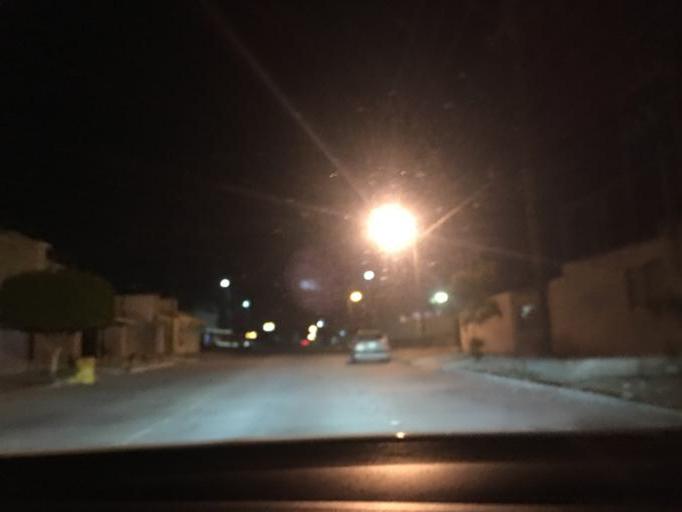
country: MX
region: Baja California Sur
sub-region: La Paz
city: La Paz
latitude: 24.1406
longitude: -110.3168
